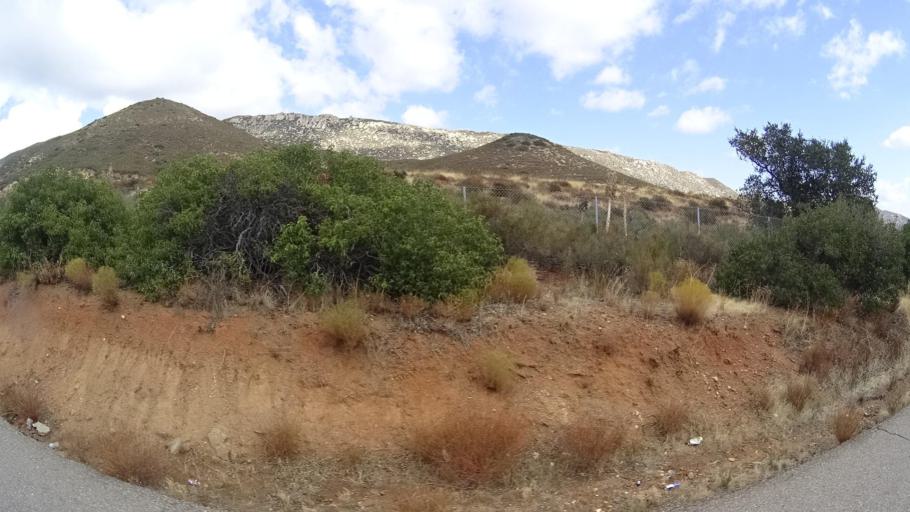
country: US
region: California
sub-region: San Diego County
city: Pine Valley
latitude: 32.7744
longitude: -116.4934
